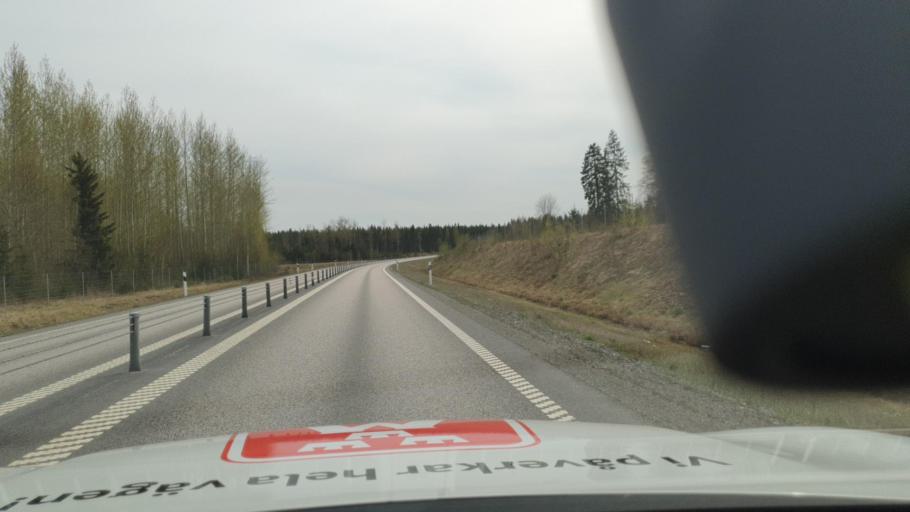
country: SE
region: Uppsala
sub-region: Heby Kommun
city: Heby
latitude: 59.9840
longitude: 16.8522
